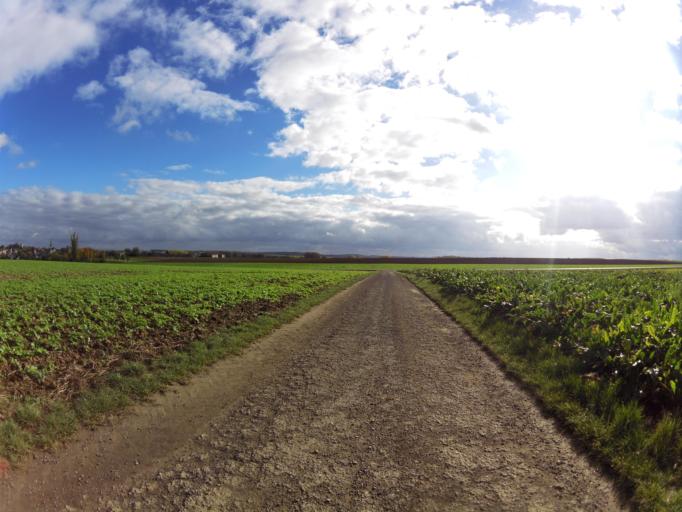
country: DE
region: Bavaria
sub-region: Regierungsbezirk Unterfranken
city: Unterpleichfeld
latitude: 49.8740
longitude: 10.0184
